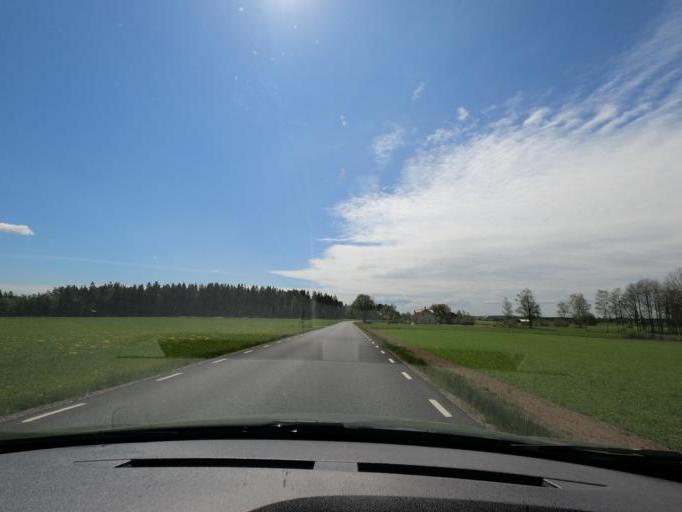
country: SE
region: Joenkoeping
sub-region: Varnamo Kommun
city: Bredaryd
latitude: 57.1397
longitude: 13.7124
